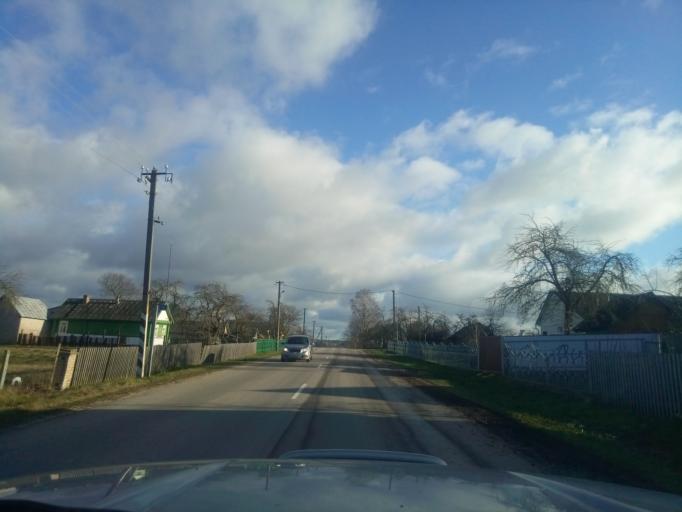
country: BY
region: Minsk
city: Tsimkavichy
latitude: 53.1758
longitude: 26.9526
